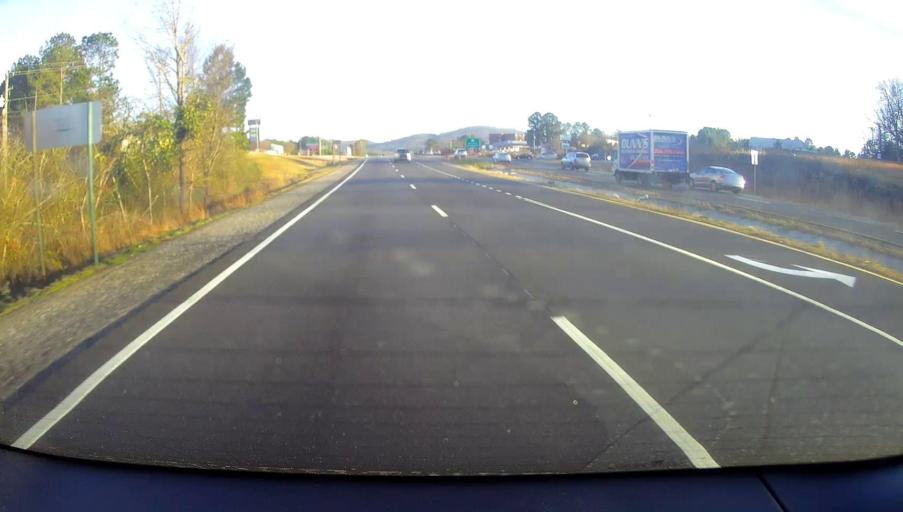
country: US
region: Alabama
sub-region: Calhoun County
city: Saks
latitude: 33.7060
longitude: -85.8346
